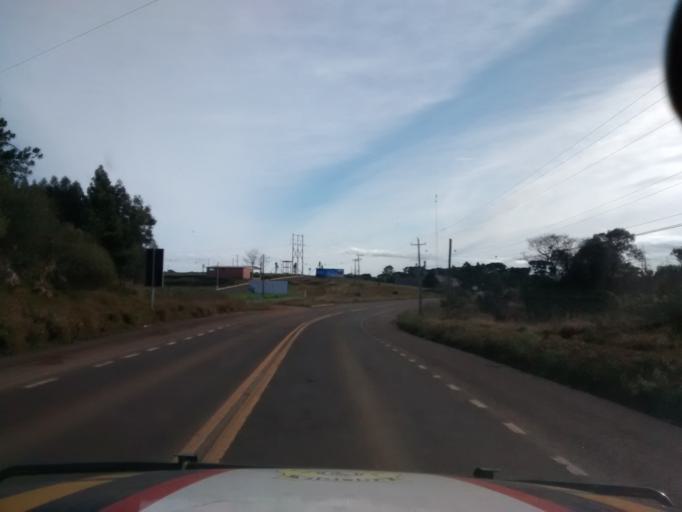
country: BR
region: Rio Grande do Sul
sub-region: Lagoa Vermelha
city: Lagoa Vermelha
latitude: -28.1916
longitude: -51.5259
